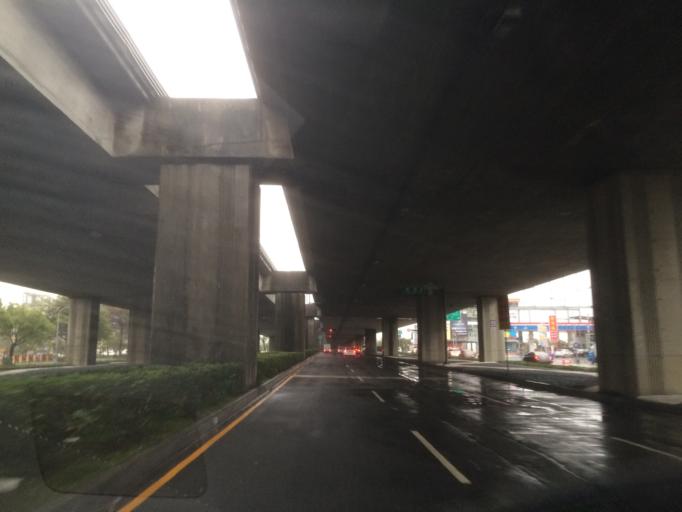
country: TW
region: Taiwan
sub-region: Taichung City
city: Taichung
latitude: 24.1469
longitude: 120.6233
